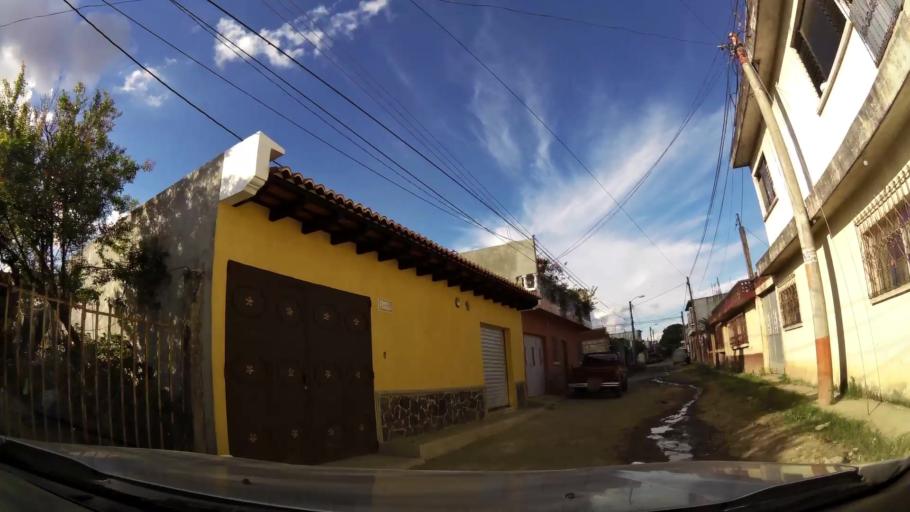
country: GT
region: Guatemala
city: Villa Nueva
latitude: 14.5269
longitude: -90.5801
